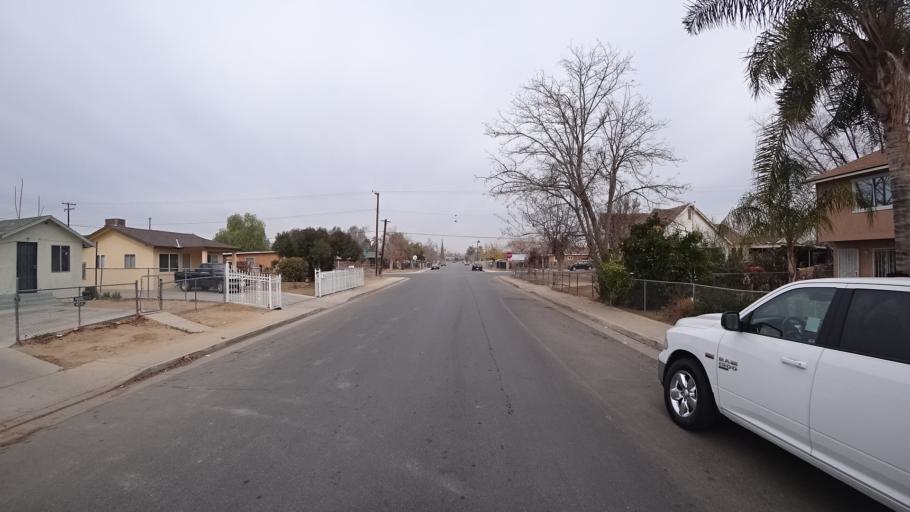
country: US
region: California
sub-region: Kern County
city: Bakersfield
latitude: 35.3644
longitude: -118.9827
